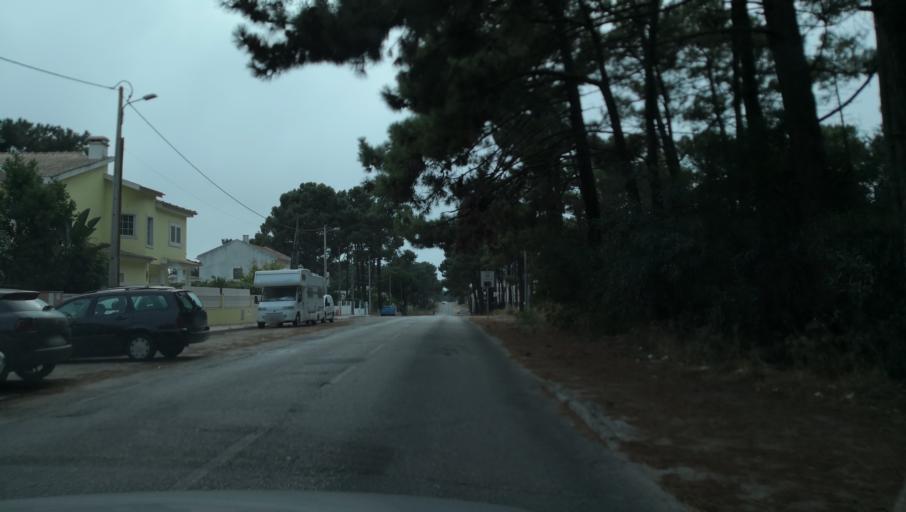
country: PT
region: Setubal
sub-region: Almada
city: Charneca
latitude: 38.5819
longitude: -9.1766
